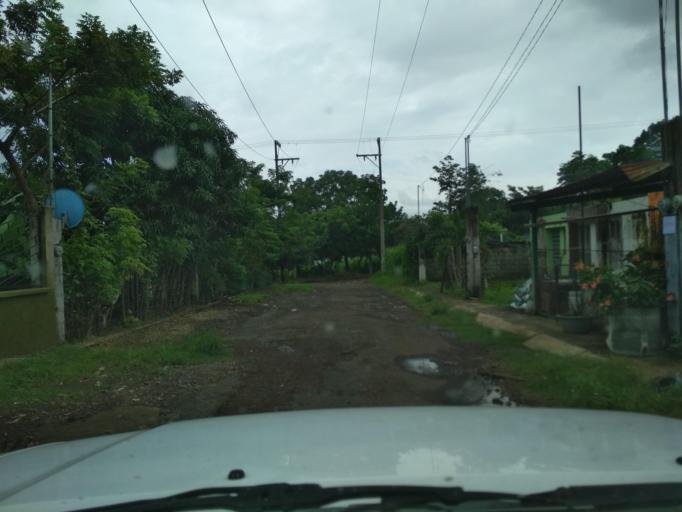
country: MX
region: Veracruz
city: Comoapan
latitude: 18.4235
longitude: -95.1797
